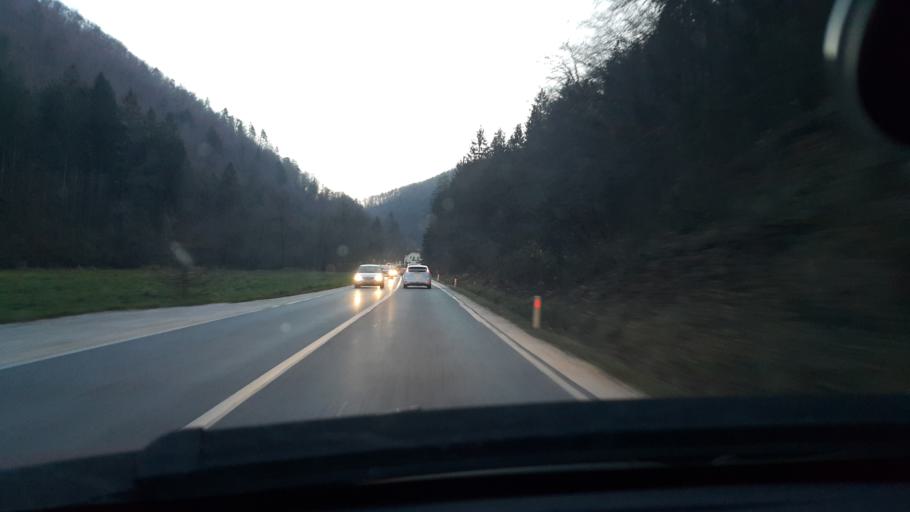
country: SI
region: Zalec
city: Gotovlje
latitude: 46.3033
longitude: 15.1725
